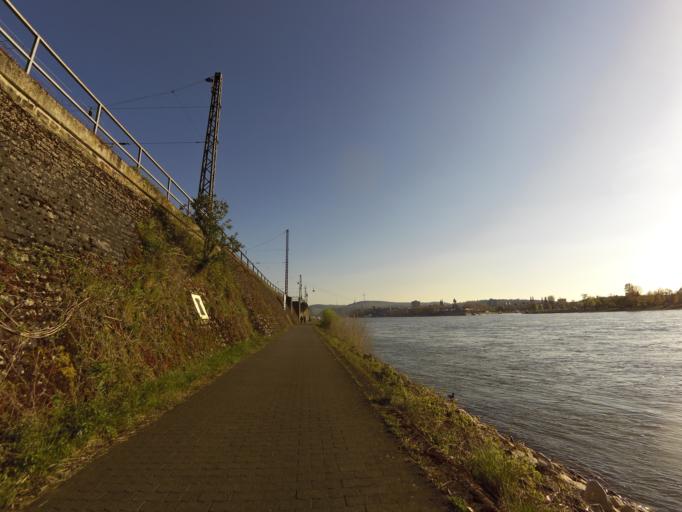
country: DE
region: Rheinland-Pfalz
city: Urbar
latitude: 50.3700
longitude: 7.6131
